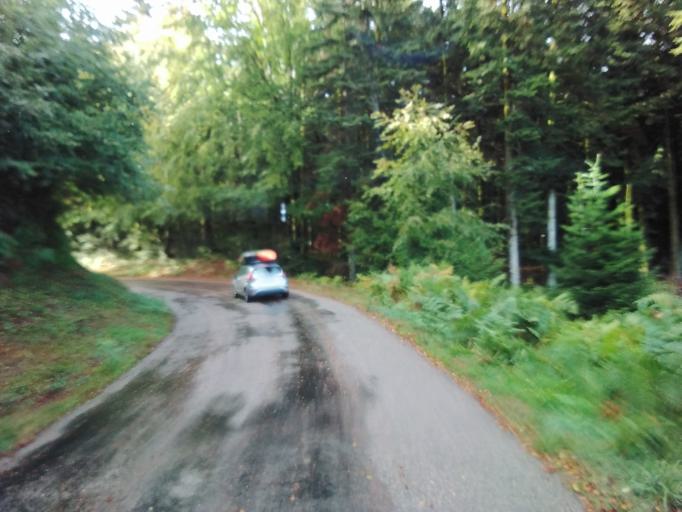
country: FR
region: Bourgogne
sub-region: Departement de la Nievre
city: Lormes
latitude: 47.2971
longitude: 3.8822
